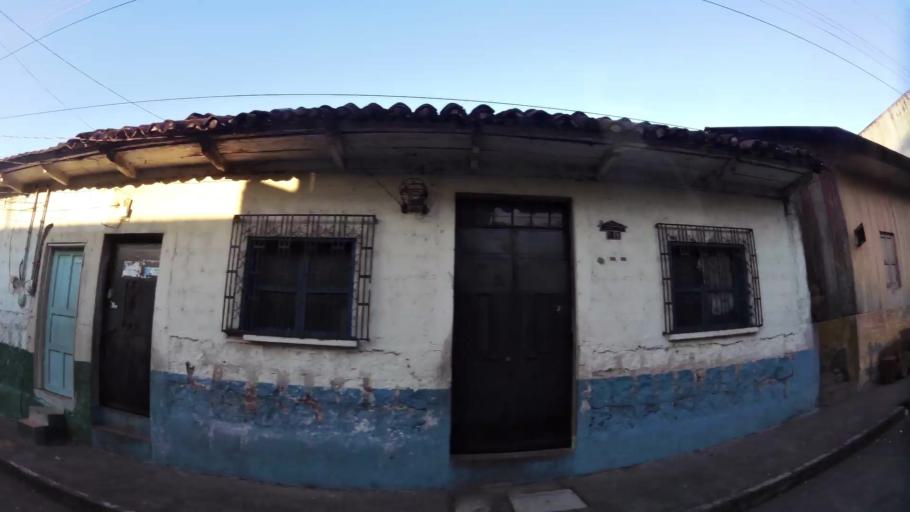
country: GT
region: Suchitepeque
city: Mazatenango
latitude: 14.5380
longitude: -91.5035
